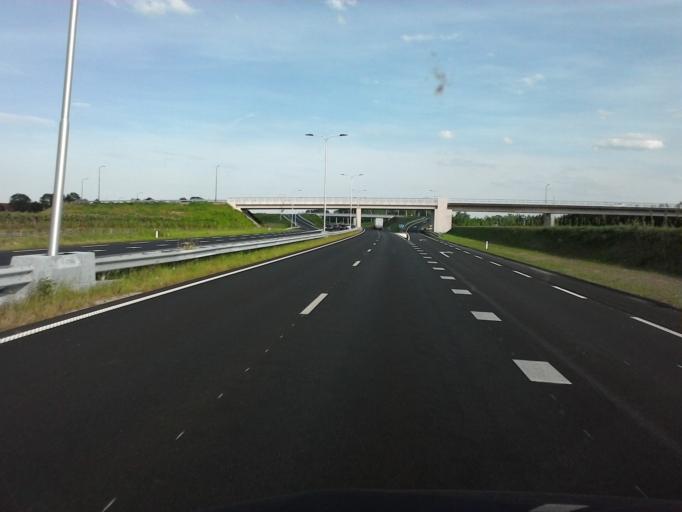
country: NL
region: North Brabant
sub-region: Gemeente Schijndel
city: Schijndel
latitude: 51.6591
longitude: 5.4088
